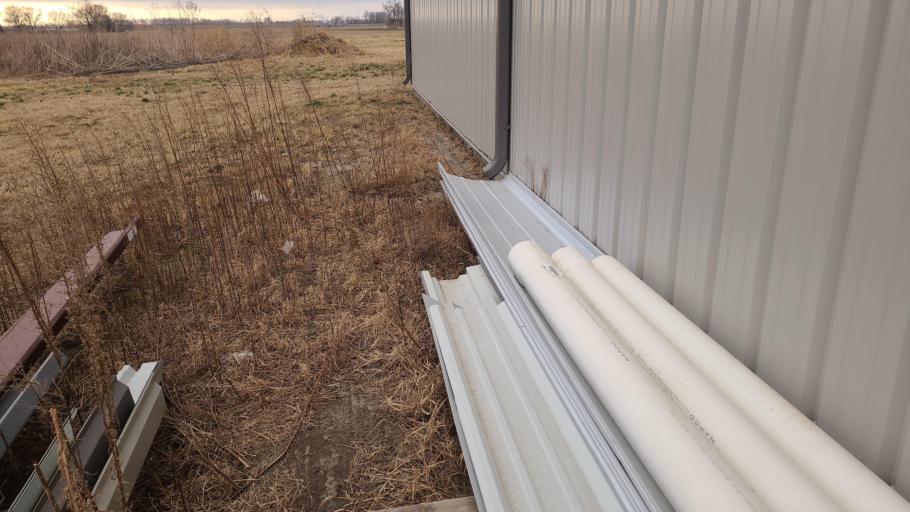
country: US
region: Kansas
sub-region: Douglas County
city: Lawrence
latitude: 39.0052
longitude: -95.2148
